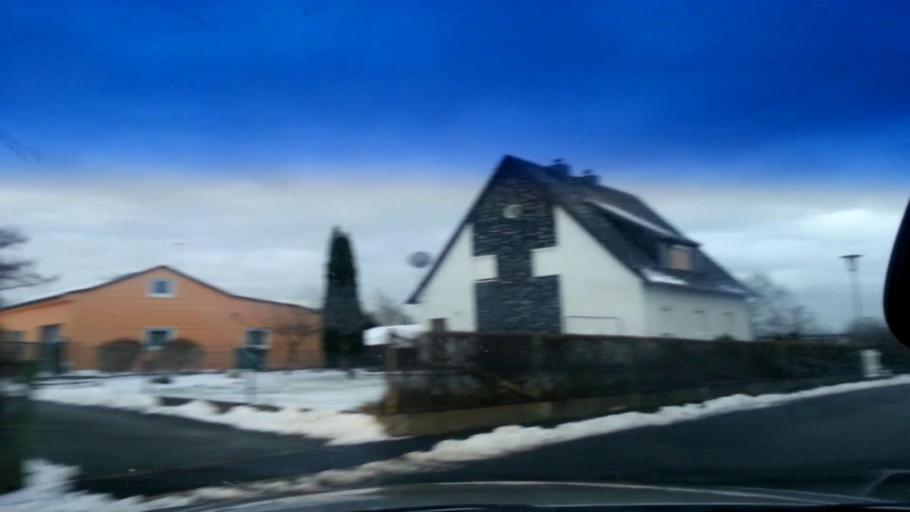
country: DE
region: Bavaria
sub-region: Upper Franconia
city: Selb
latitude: 50.1756
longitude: 12.1256
